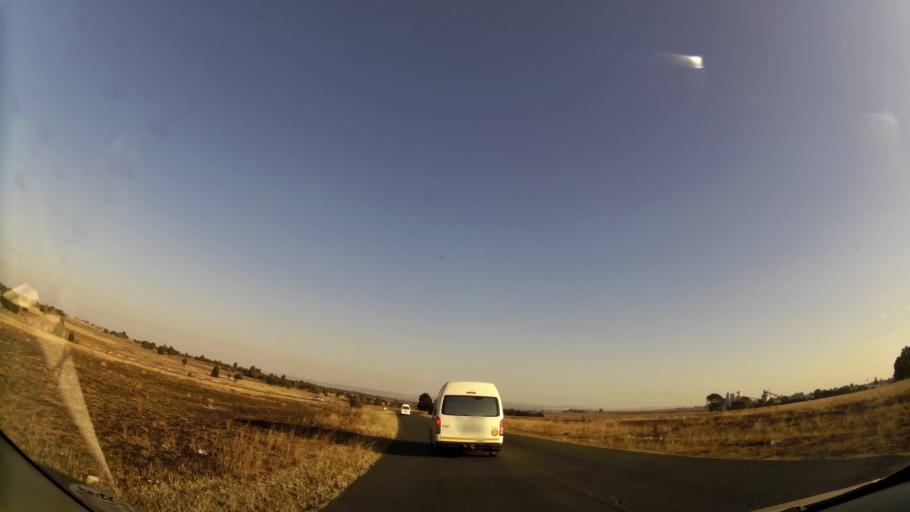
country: ZA
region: Gauteng
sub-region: West Rand District Municipality
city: Randfontein
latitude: -26.2007
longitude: 27.6749
